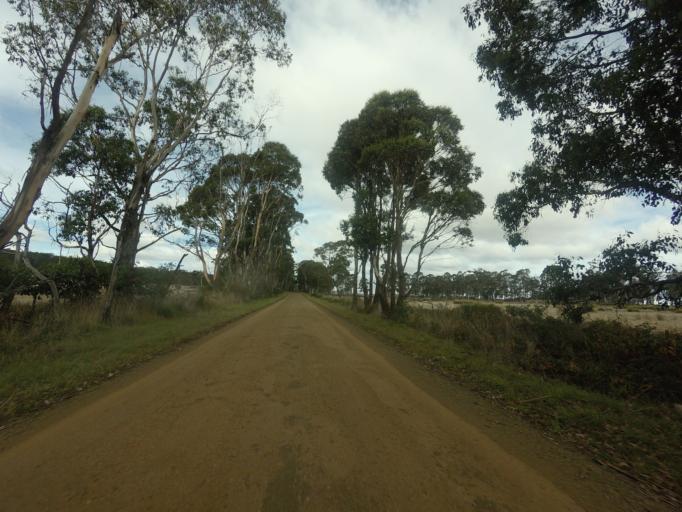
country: AU
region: Tasmania
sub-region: Brighton
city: Bridgewater
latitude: -42.4219
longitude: 147.4230
